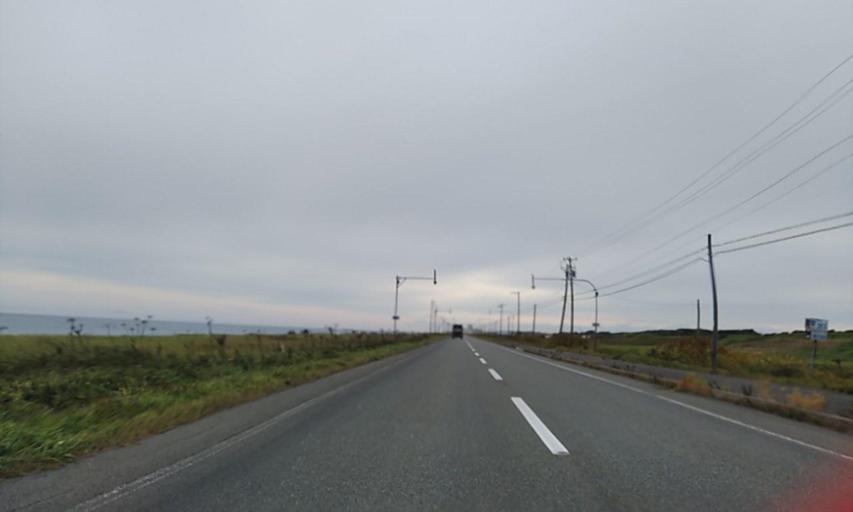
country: JP
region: Hokkaido
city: Makubetsu
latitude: 45.3587
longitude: 142.1303
